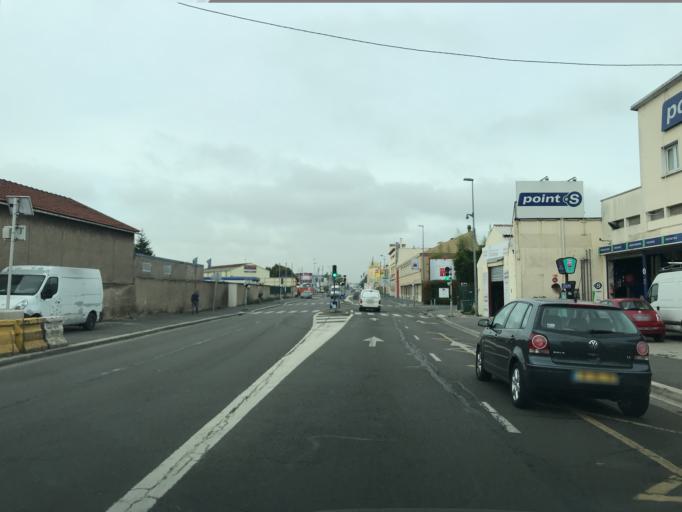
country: FR
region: Ile-de-France
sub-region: Departement de Seine-Saint-Denis
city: Bobigny
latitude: 48.9088
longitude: 2.4282
